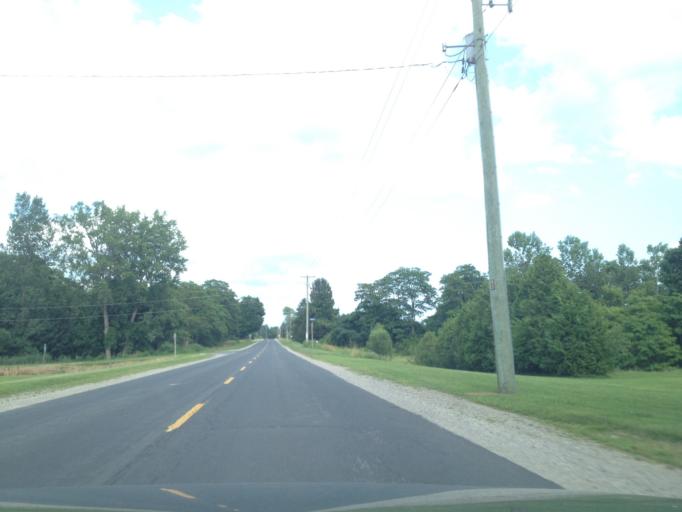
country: CA
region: Ontario
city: Aylmer
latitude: 42.6744
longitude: -80.9117
